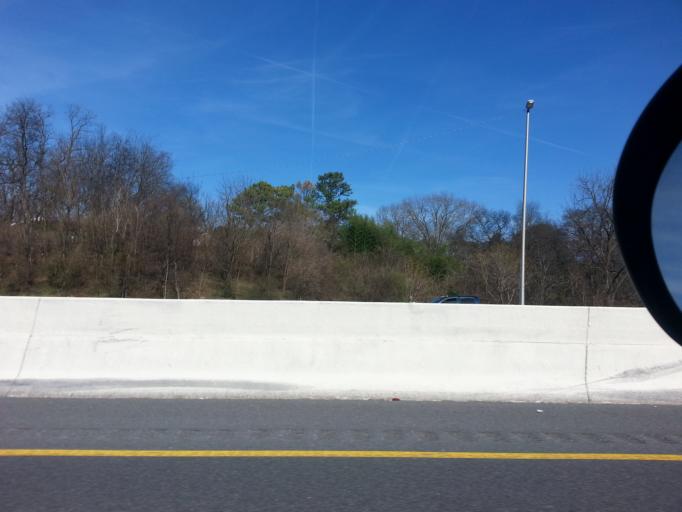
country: US
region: Tennessee
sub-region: Davidson County
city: Oak Hill
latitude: 36.0794
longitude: -86.6961
